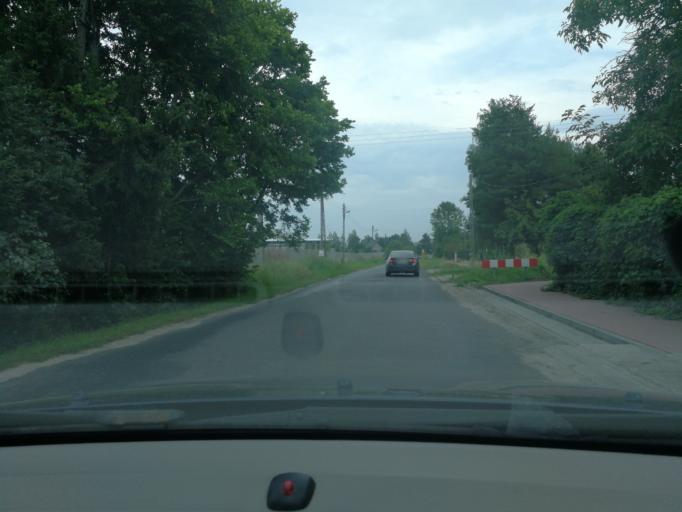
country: PL
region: Masovian Voivodeship
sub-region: Powiat grodziski
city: Grodzisk Mazowiecki
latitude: 52.1305
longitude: 20.5972
